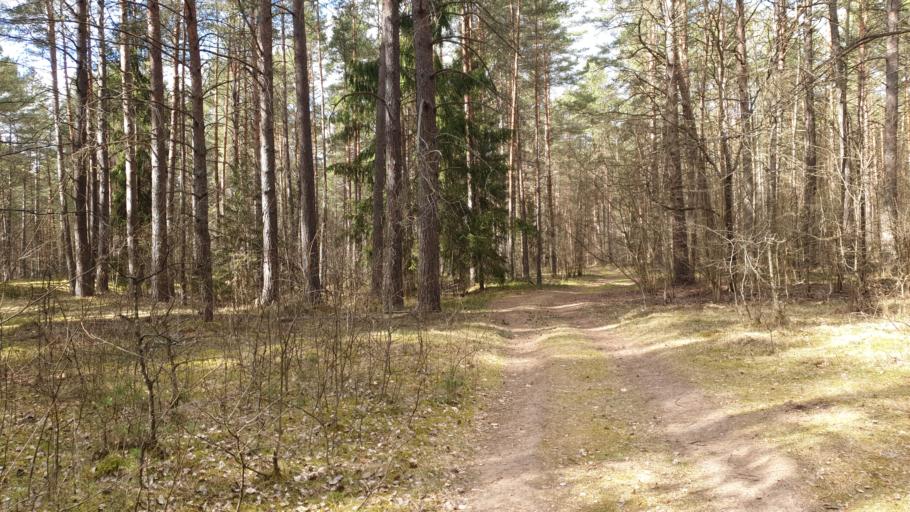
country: LT
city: Grigiskes
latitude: 54.7276
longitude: 25.0323
